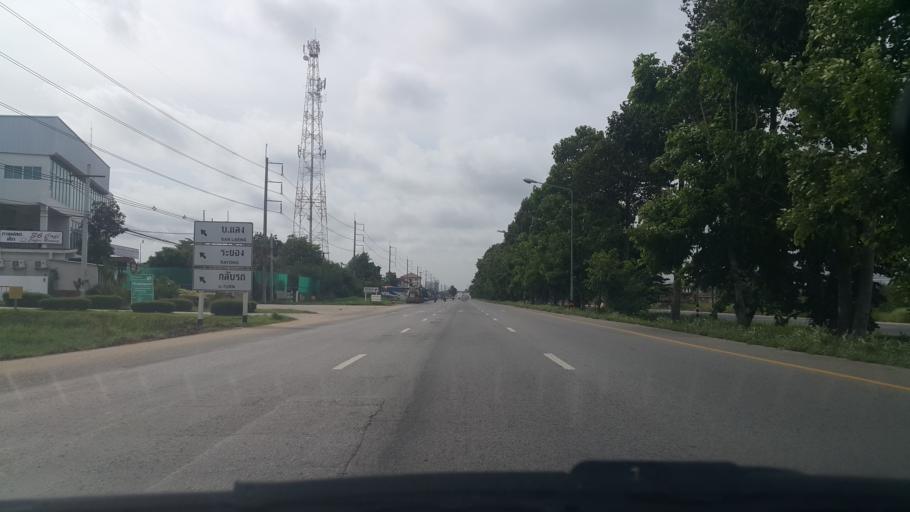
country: TH
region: Rayong
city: Rayong
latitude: 12.6762
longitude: 101.3030
